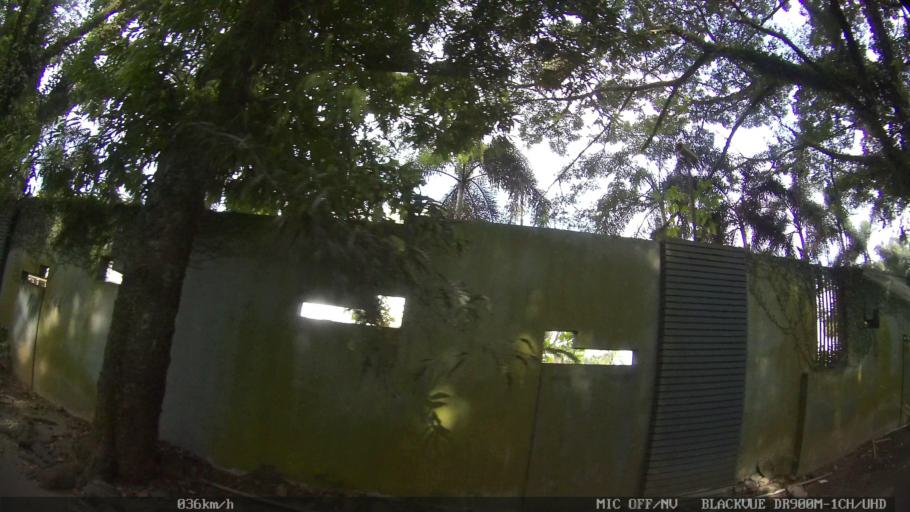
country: ID
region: North Sumatra
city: Medan
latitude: 3.5661
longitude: 98.6837
